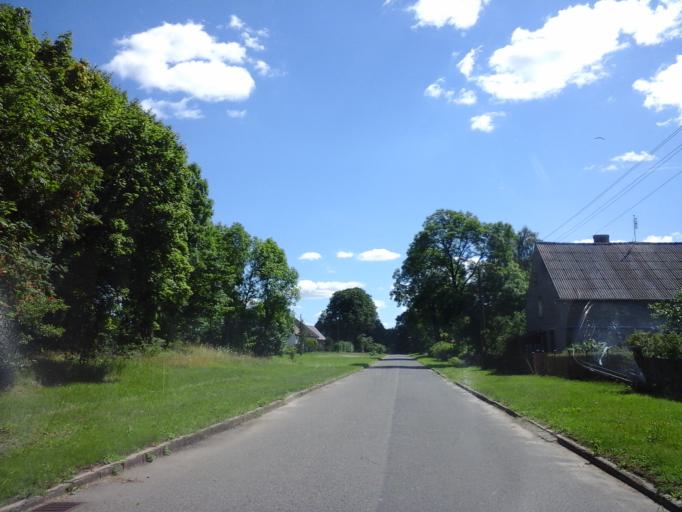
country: PL
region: West Pomeranian Voivodeship
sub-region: Powiat choszczenski
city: Drawno
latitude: 53.2840
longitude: 15.6853
